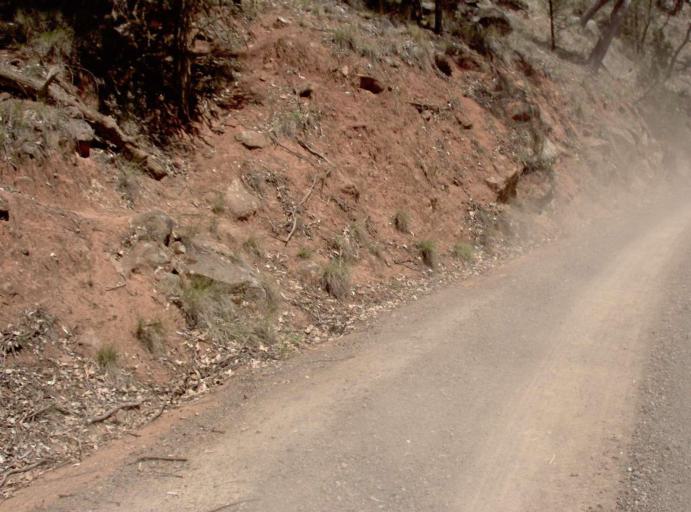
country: AU
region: New South Wales
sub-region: Snowy River
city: Jindabyne
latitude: -37.0656
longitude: 148.5047
